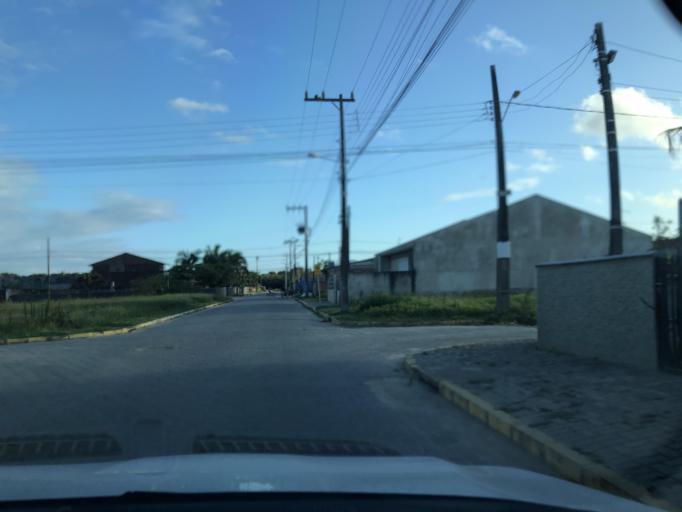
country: BR
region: Santa Catarina
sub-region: Sao Francisco Do Sul
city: Sao Francisco do Sul
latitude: -26.2339
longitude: -48.5238
